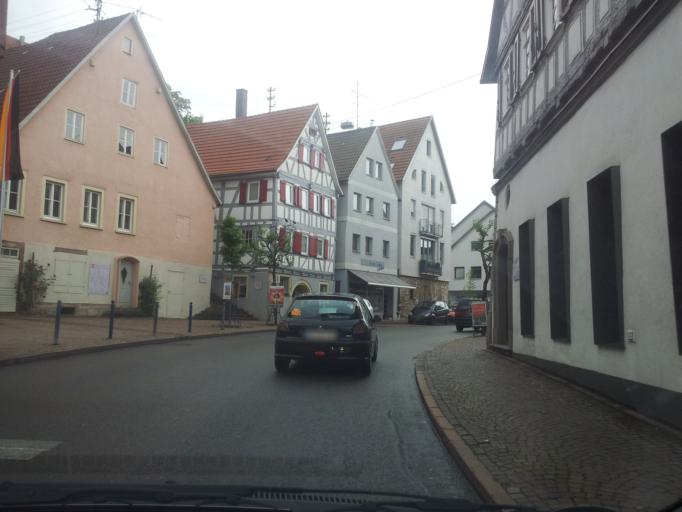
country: DE
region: Baden-Wuerttemberg
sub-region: Regierungsbezirk Stuttgart
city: Beilstein
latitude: 49.0408
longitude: 9.3141
